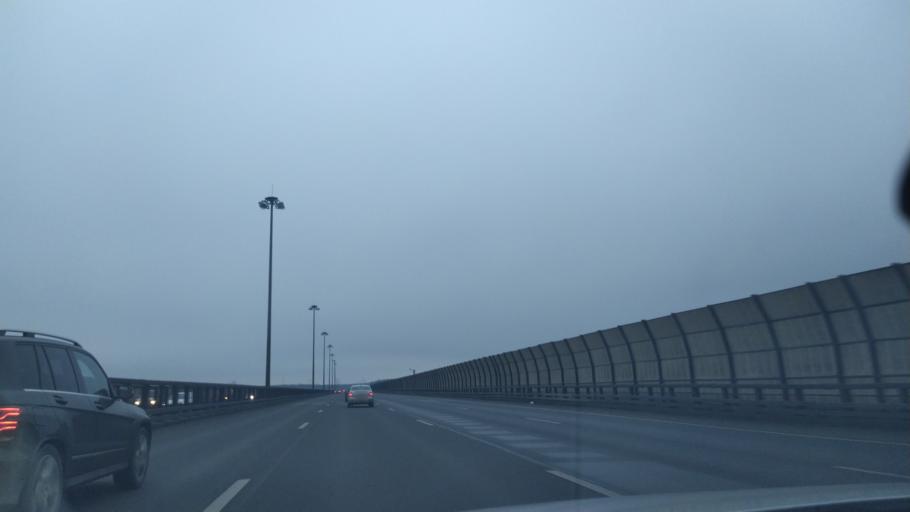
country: RU
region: St.-Petersburg
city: Krasnogvargeisky
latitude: 59.9794
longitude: 30.5248
